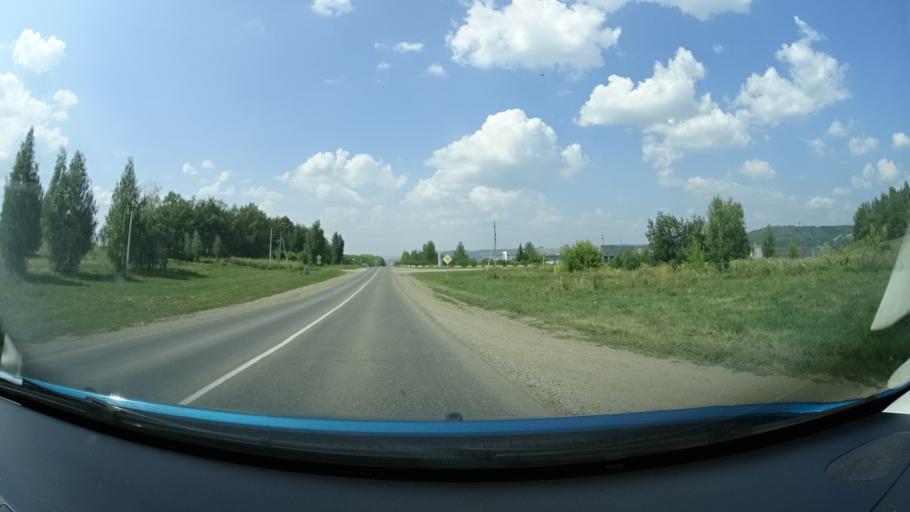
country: RU
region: Bashkortostan
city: Oktyabr'skiy
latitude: 54.4789
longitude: 53.5632
